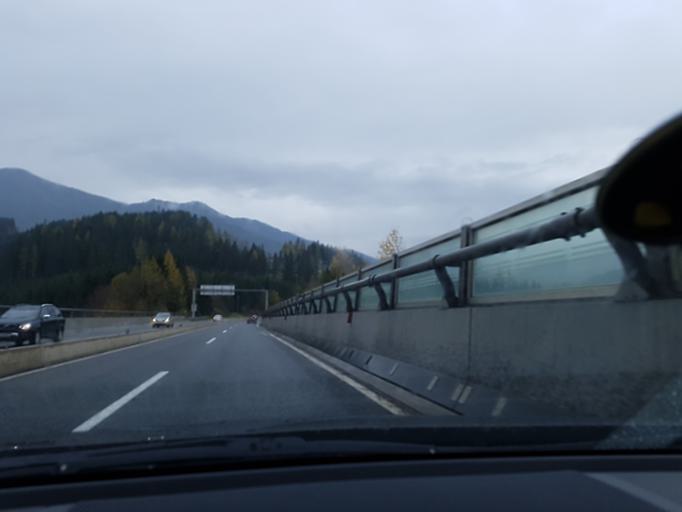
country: AT
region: Salzburg
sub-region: Politischer Bezirk Sankt Johann im Pongau
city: Bischofshofen
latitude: 47.4361
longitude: 13.2247
